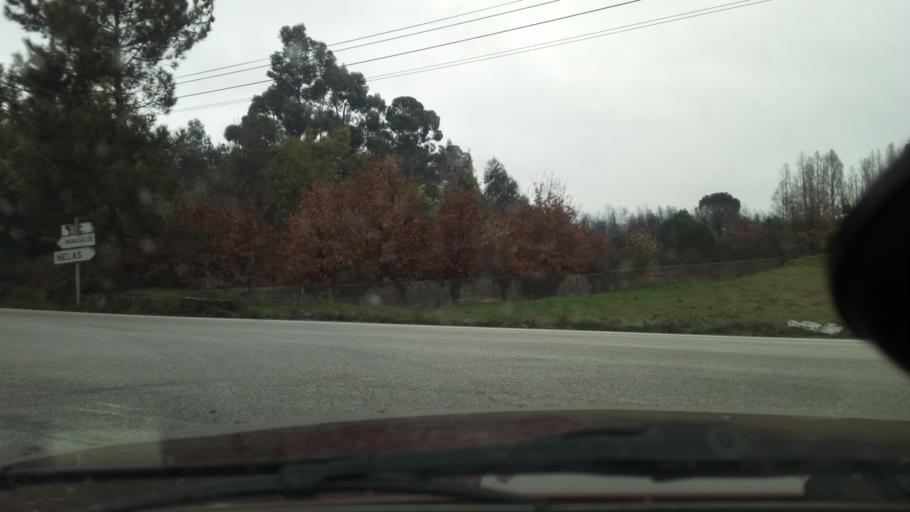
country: PT
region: Viseu
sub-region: Mangualde
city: Mangualde
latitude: 40.6017
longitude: -7.7898
